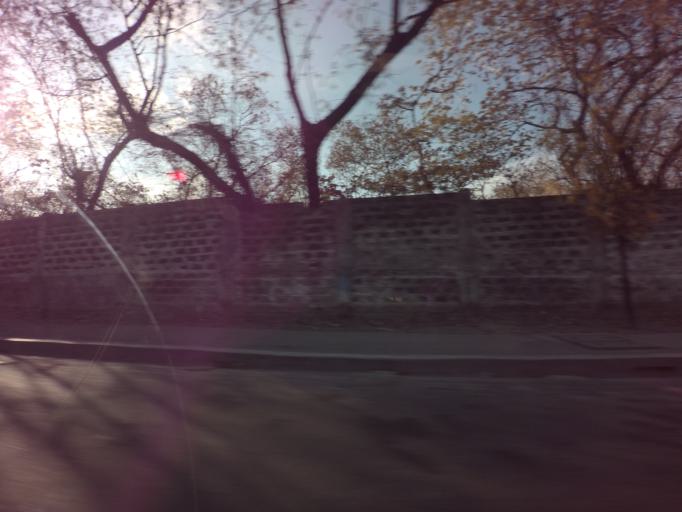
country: PH
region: Calabarzon
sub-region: Province of Rizal
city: Taguig
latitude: 14.4889
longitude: 121.0510
